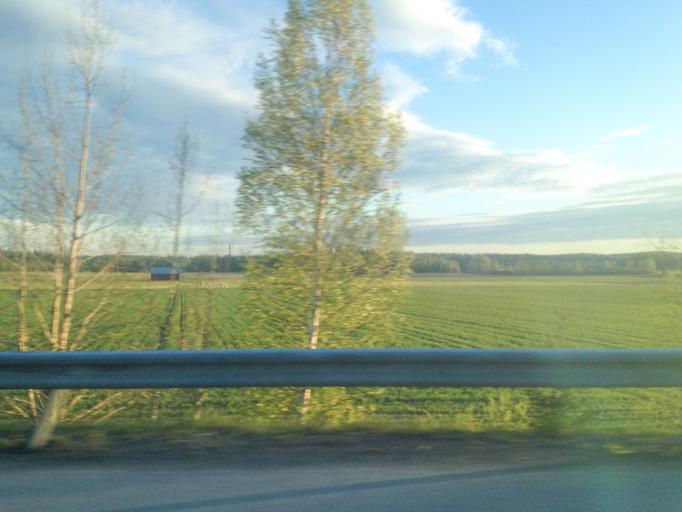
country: FI
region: Haeme
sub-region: Haemeenlinna
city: Tervakoski
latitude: 60.8281
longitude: 24.6607
